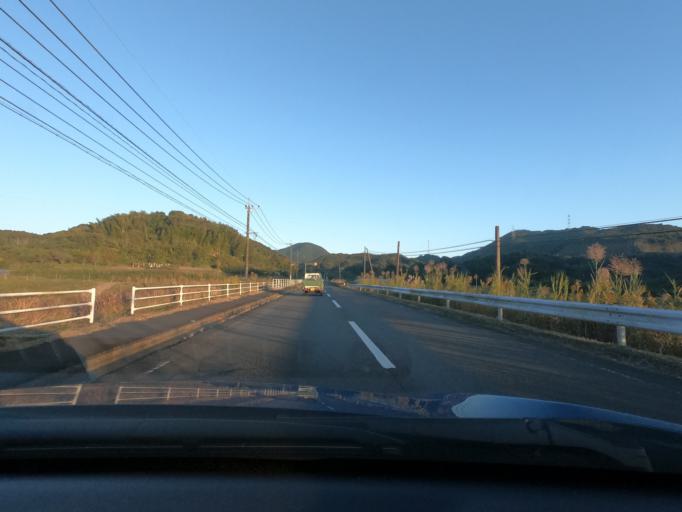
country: JP
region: Kagoshima
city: Satsumasendai
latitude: 31.7909
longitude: 130.4612
